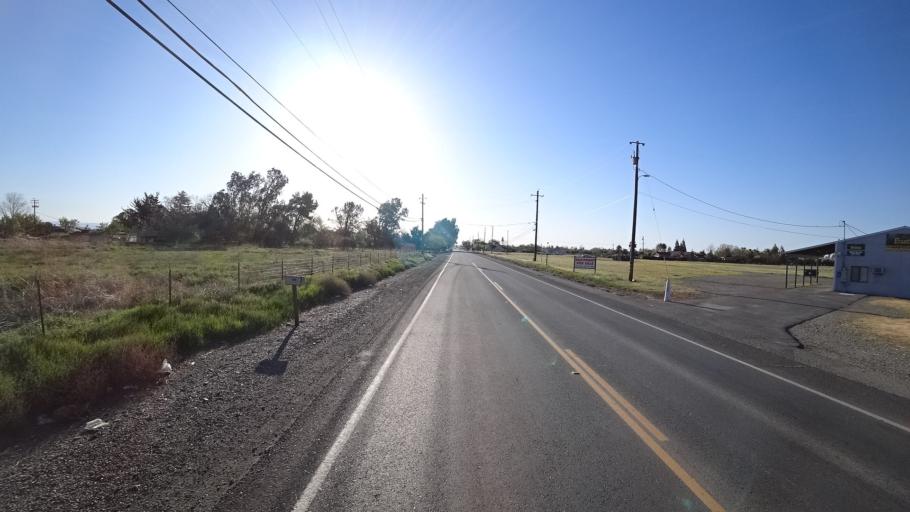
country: US
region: California
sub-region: Glenn County
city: Orland
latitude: 39.7541
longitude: -122.2138
